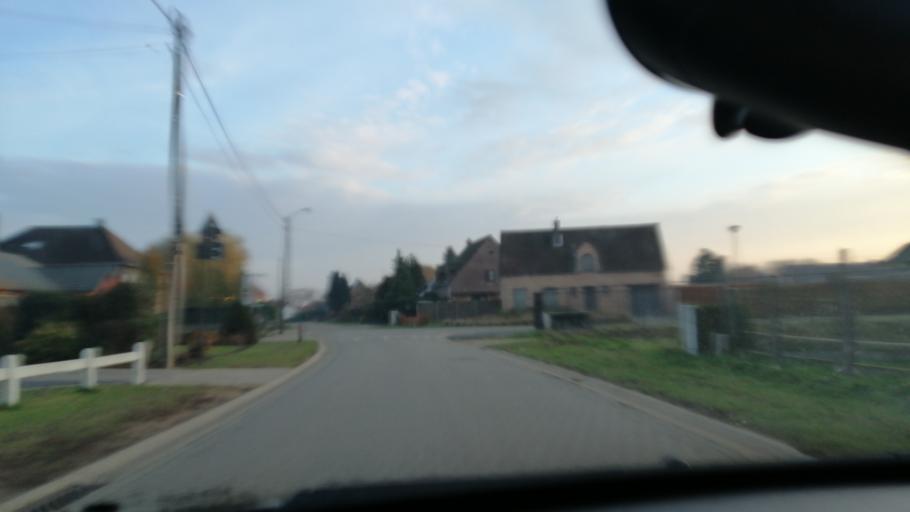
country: BE
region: Flanders
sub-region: Provincie Antwerpen
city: Lille
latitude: 51.2410
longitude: 4.8180
